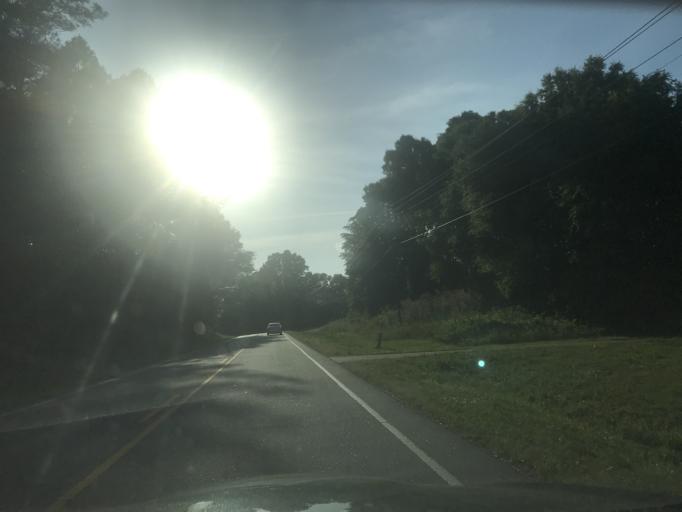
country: US
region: North Carolina
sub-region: Wake County
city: Knightdale
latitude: 35.7517
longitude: -78.4873
